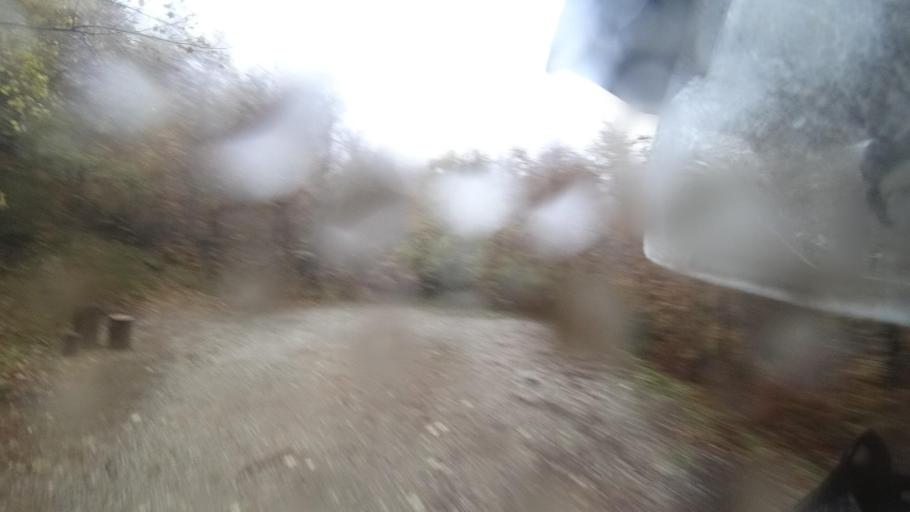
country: HR
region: Primorsko-Goranska
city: Vrbovsko
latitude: 45.2765
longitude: 14.9770
